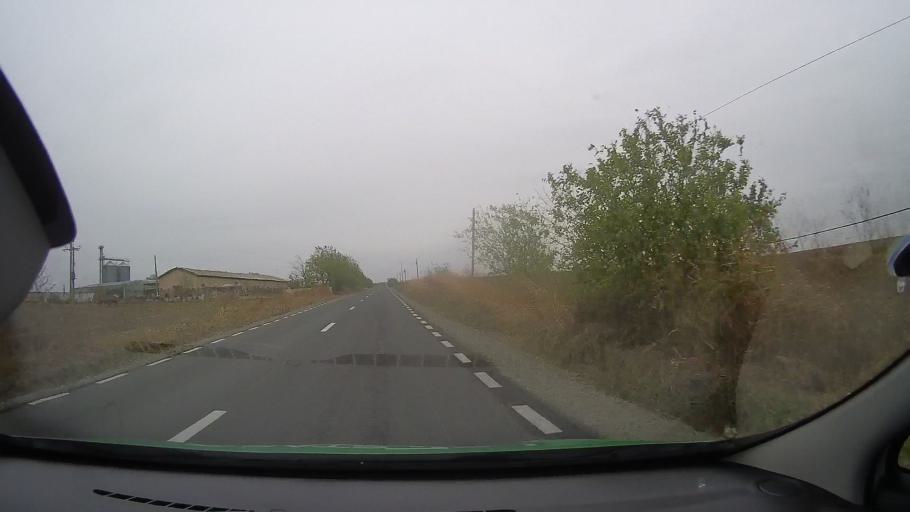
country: RO
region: Constanta
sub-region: Comuna Tortoman
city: Tortoman
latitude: 44.3629
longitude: 28.2095
